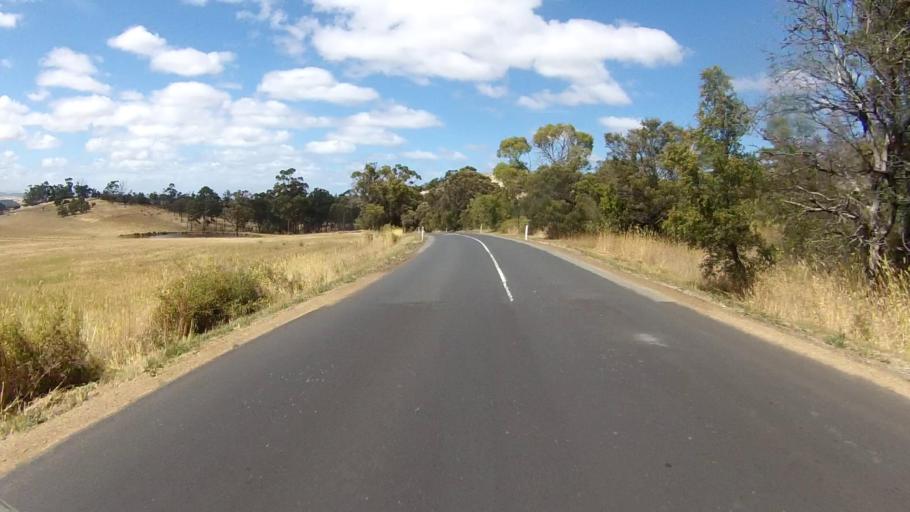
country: AU
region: Tasmania
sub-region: Sorell
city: Sorell
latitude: -42.7418
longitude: 147.4837
